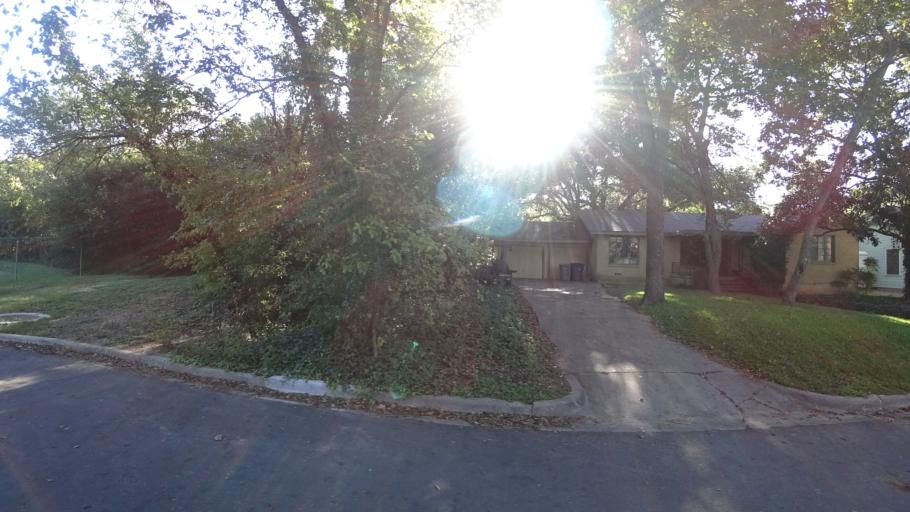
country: US
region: Texas
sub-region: Travis County
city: Austin
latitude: 30.3115
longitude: -97.7266
